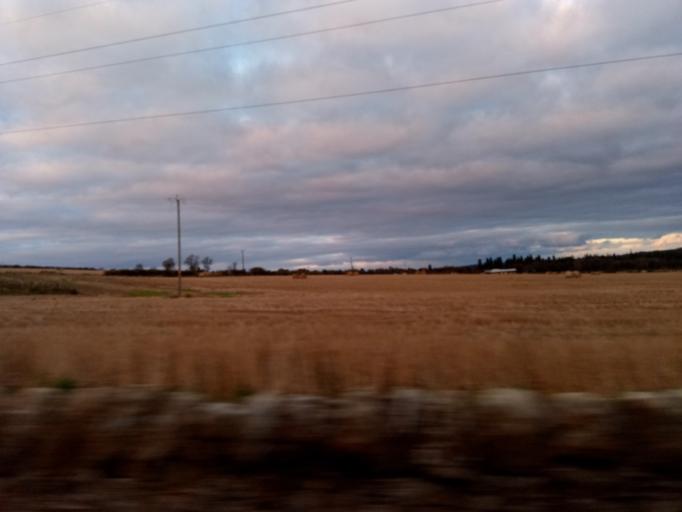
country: GB
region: Scotland
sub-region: Fife
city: Pathhead
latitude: 55.8726
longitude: -2.9952
